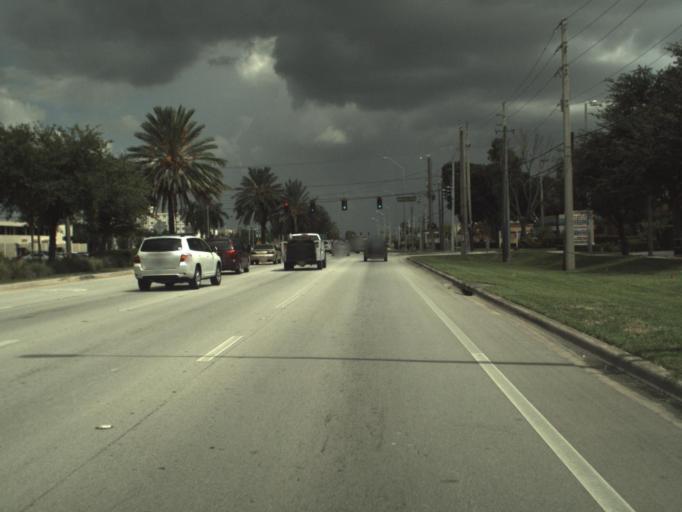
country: US
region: Florida
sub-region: Broward County
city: Margate
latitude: 26.2578
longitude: -80.2014
